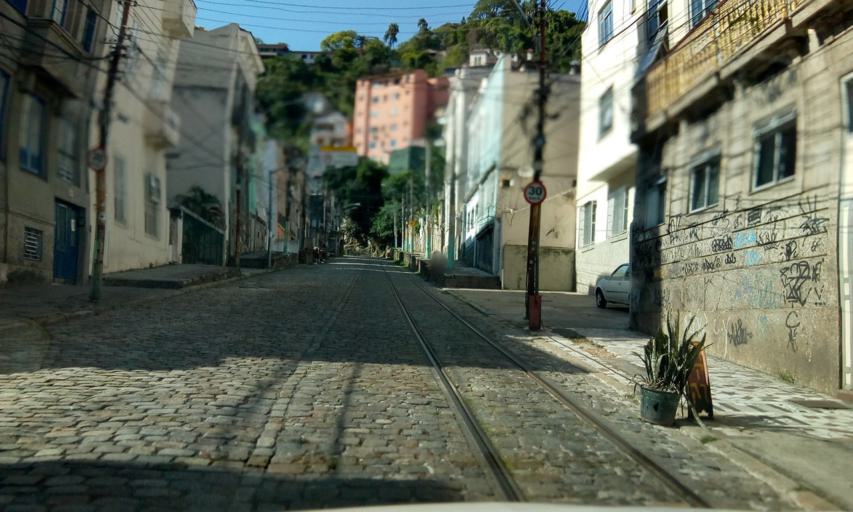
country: BR
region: Rio de Janeiro
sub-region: Rio De Janeiro
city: Rio de Janeiro
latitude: -22.9150
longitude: -43.1826
